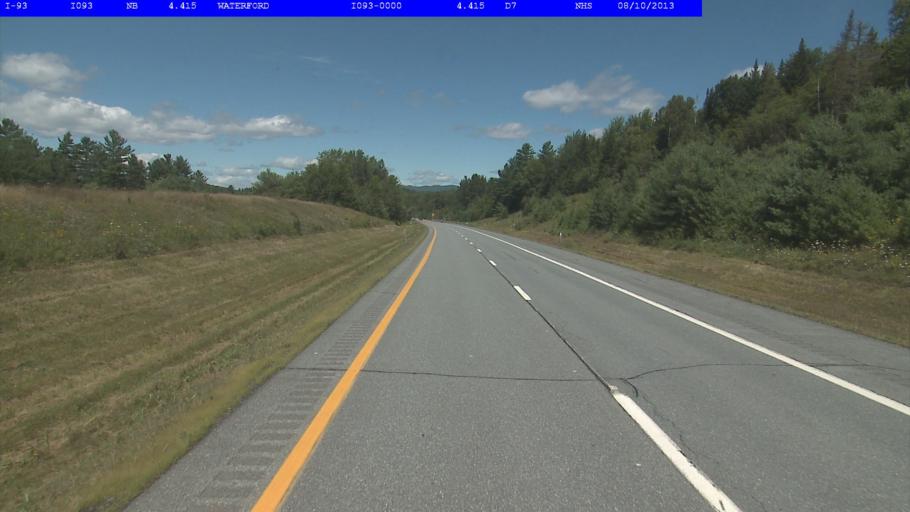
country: US
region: Vermont
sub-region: Caledonia County
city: Saint Johnsbury
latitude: 44.3990
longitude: -71.9192
